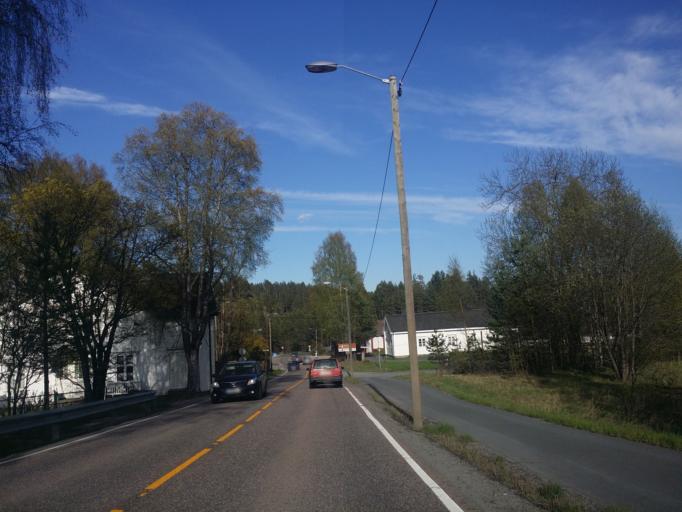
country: NO
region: Buskerud
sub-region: Kongsberg
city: Kongsberg
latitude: 59.6248
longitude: 9.6026
